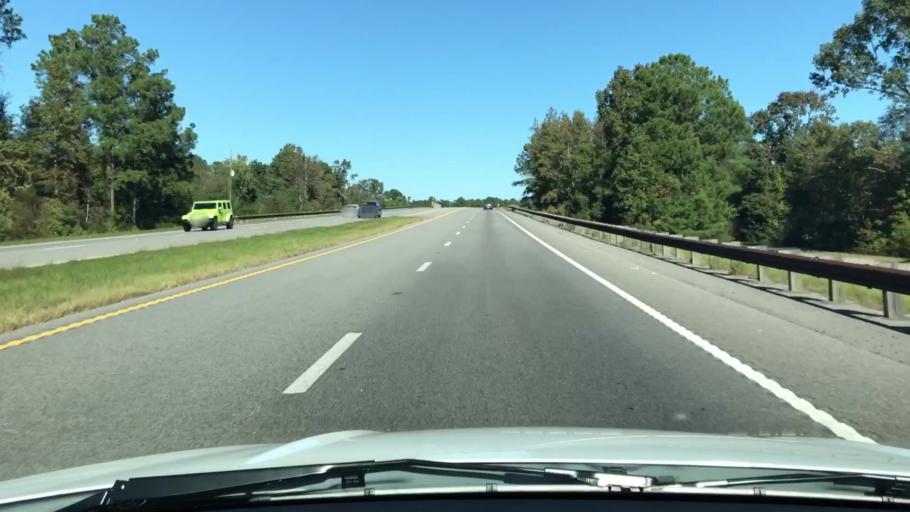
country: US
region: South Carolina
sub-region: Colleton County
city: Walterboro
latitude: 32.7322
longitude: -80.5949
